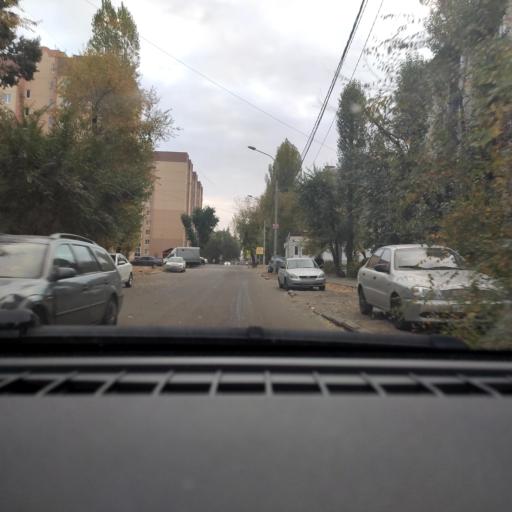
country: RU
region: Voronezj
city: Maslovka
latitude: 51.6128
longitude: 39.2314
